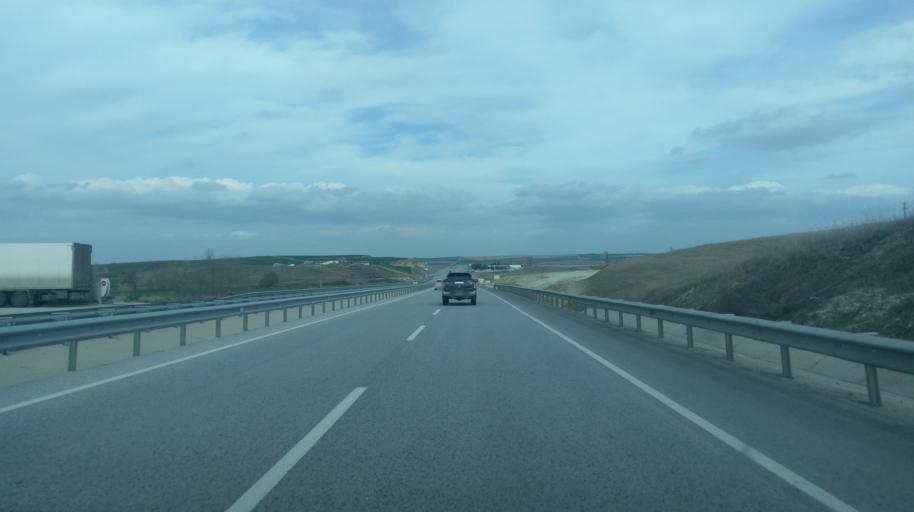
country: TR
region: Edirne
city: Kircasalih
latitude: 41.4039
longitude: 26.8148
